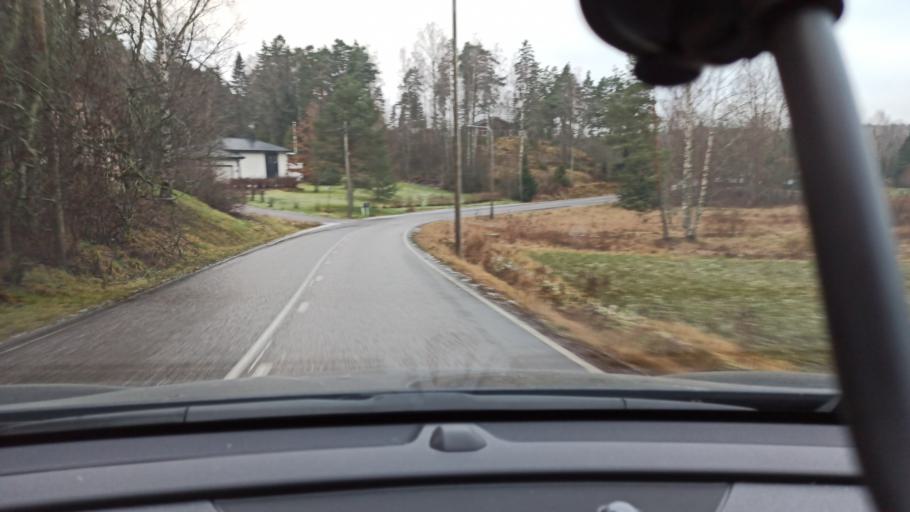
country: FI
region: Uusimaa
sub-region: Helsinki
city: Kirkkonummi
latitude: 60.1534
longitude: 24.4693
